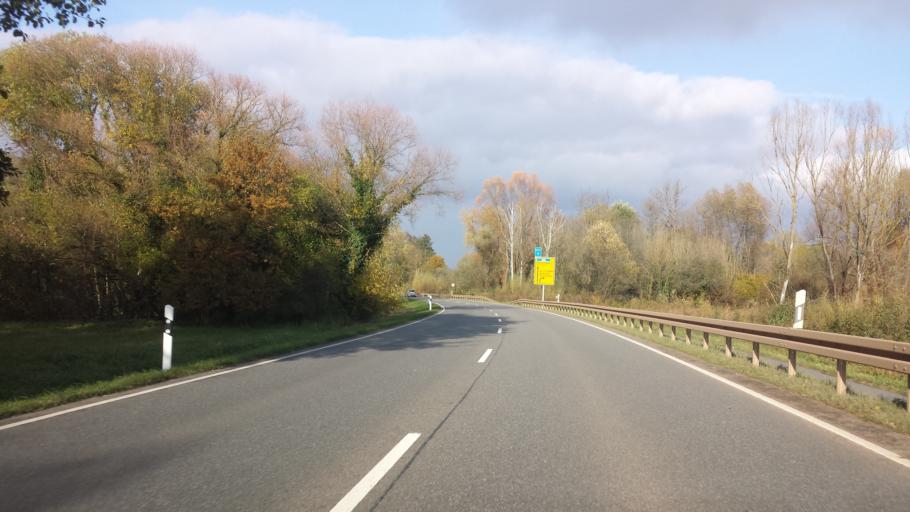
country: DE
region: Baden-Wuerttemberg
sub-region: Karlsruhe Region
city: Malsch
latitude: 49.2571
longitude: 8.6684
